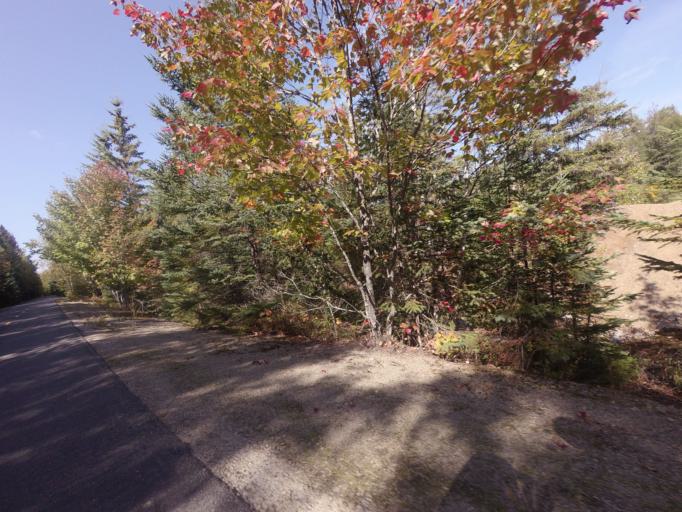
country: CA
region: Quebec
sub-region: Laurentides
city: Mont-Tremblant
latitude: 46.1246
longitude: -74.5255
